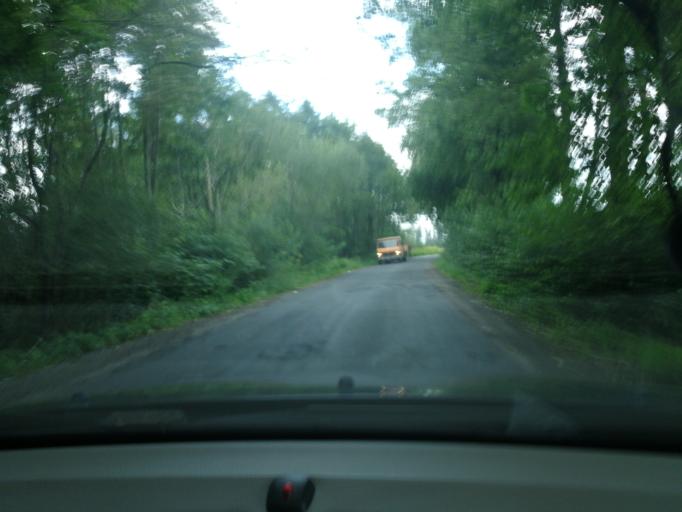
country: PL
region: Masovian Voivodeship
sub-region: Powiat warszawski zachodni
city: Bieniewice
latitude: 52.1141
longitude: 20.5554
